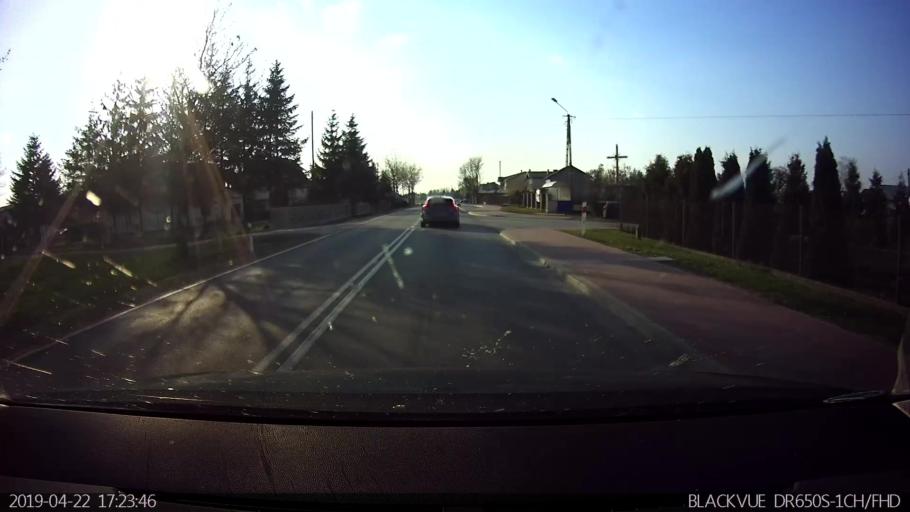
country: PL
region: Masovian Voivodeship
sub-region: Powiat sokolowski
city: Sokolow Podlaski
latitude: 52.3929
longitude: 22.3122
